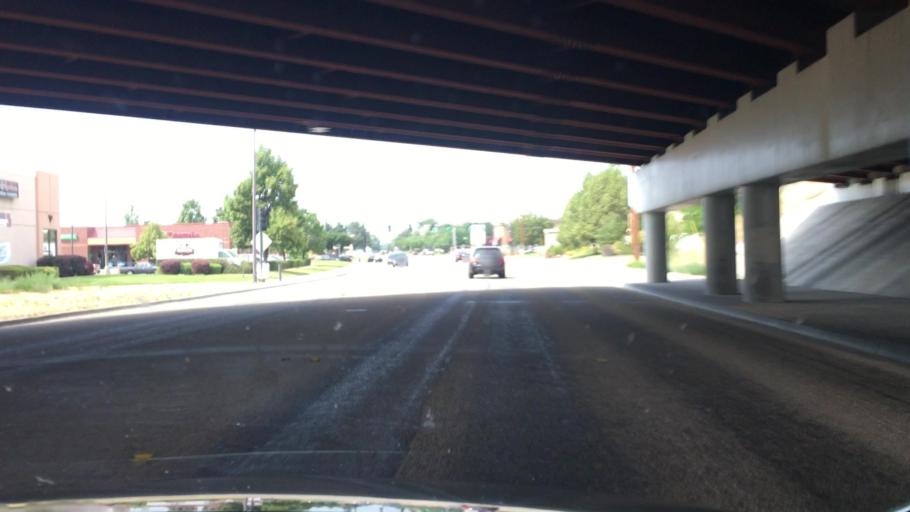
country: US
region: Idaho
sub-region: Ada County
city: Garden City
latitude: 43.6075
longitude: -116.2740
